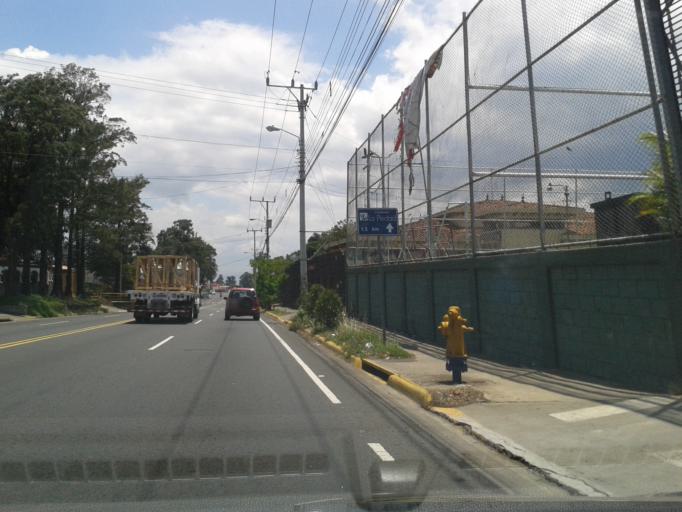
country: CR
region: Heredia
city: San Francisco
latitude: 9.9962
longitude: -84.1296
